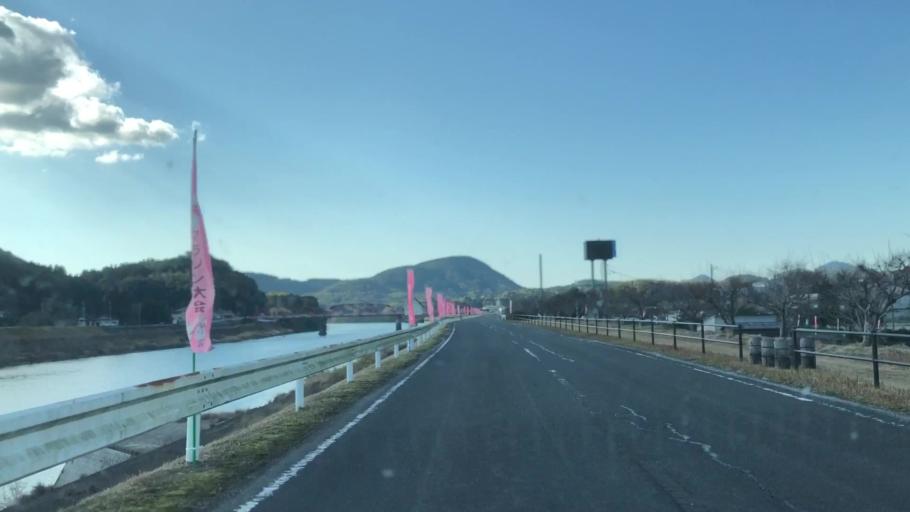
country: JP
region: Kagoshima
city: Satsumasendai
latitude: 31.8609
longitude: 130.3424
